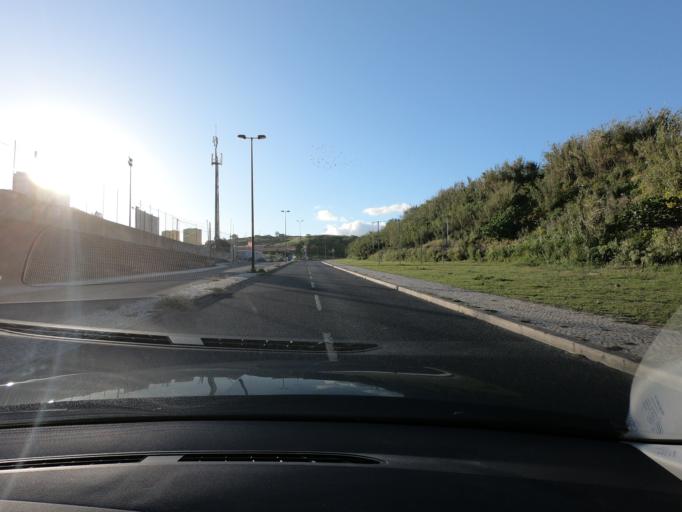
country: PT
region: Lisbon
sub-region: Lisbon
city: Lisbon
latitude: 38.7220
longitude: -9.1204
